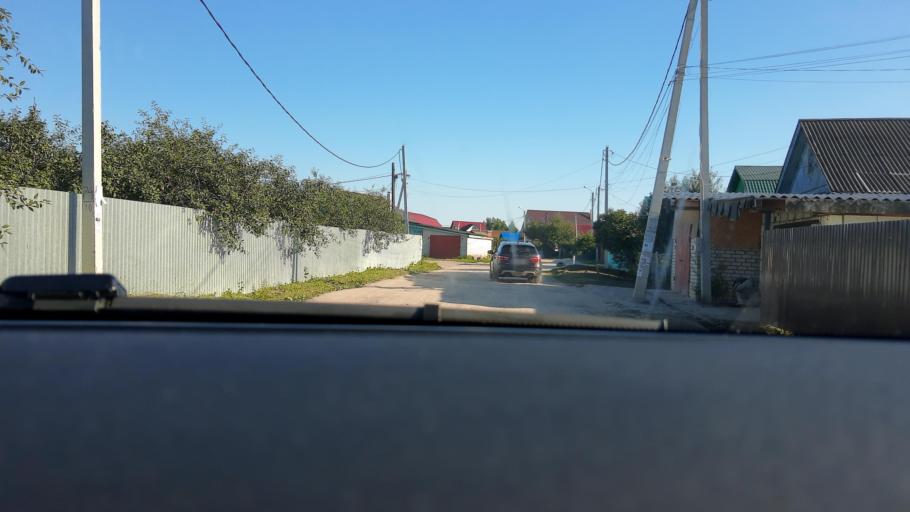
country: RU
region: Nizjnij Novgorod
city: Neklyudovo
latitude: 56.4074
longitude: 44.0339
